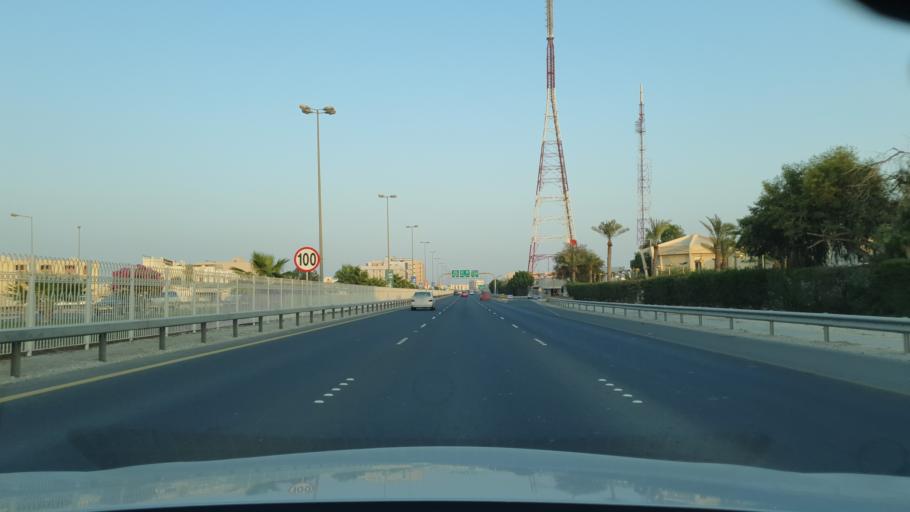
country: BH
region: Northern
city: Madinat `Isa
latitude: 26.1647
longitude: 50.5544
